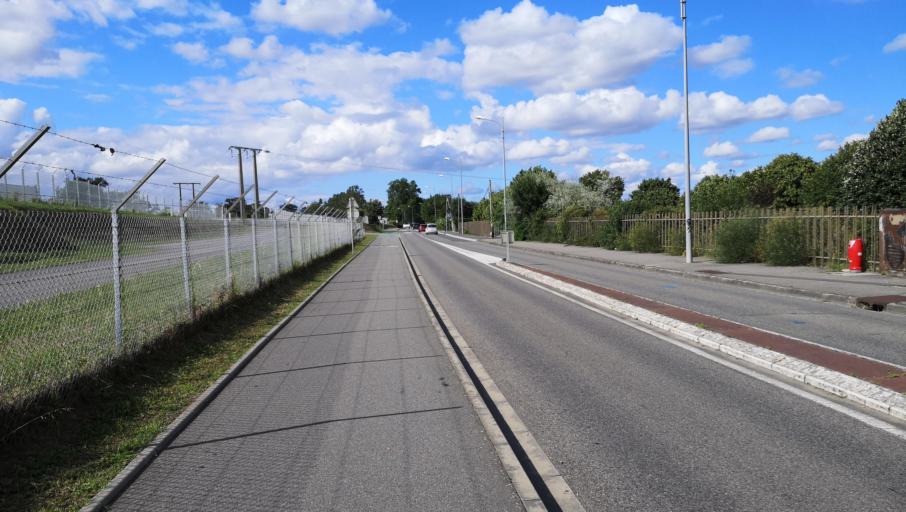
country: FR
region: Midi-Pyrenees
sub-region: Departement de la Haute-Garonne
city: Blagnac
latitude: 43.6163
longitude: 1.3877
